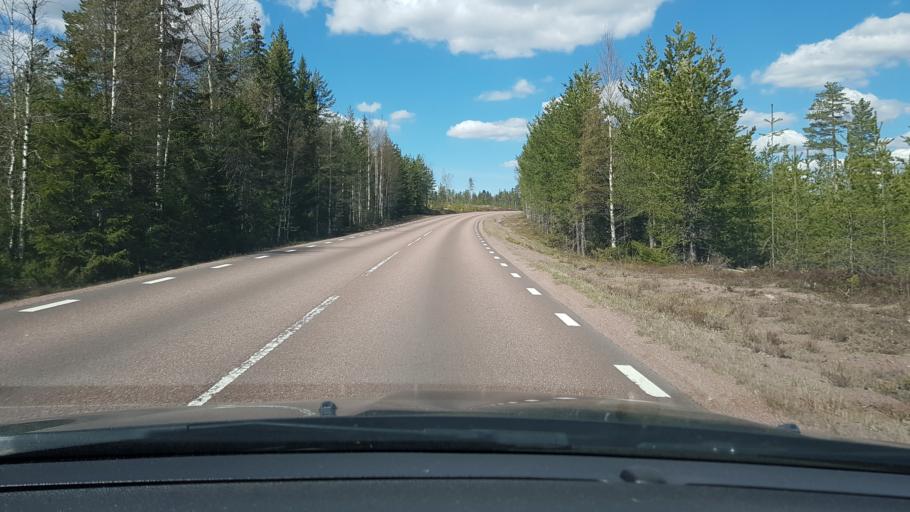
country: SE
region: Dalarna
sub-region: Malung-Saelens kommun
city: Malung
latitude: 61.0718
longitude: 13.6414
